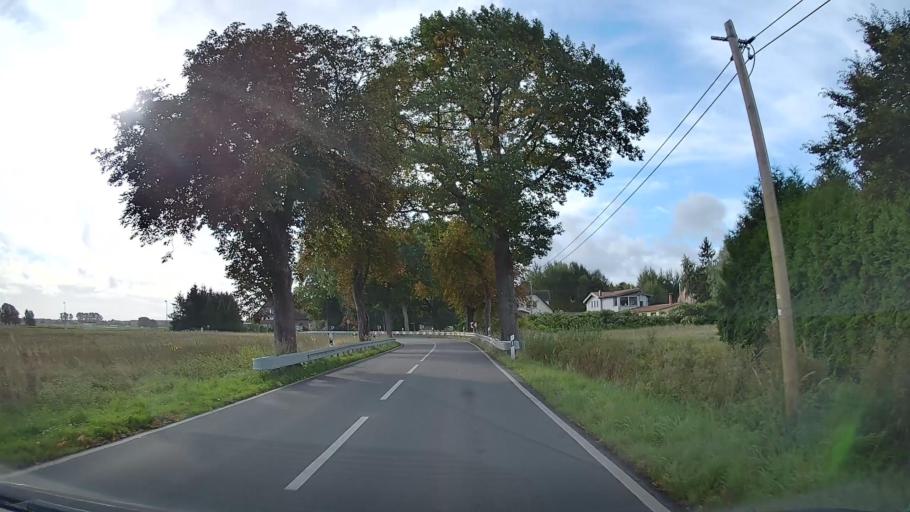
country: DE
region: Mecklenburg-Vorpommern
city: Gelbensande
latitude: 54.2380
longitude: 12.3173
